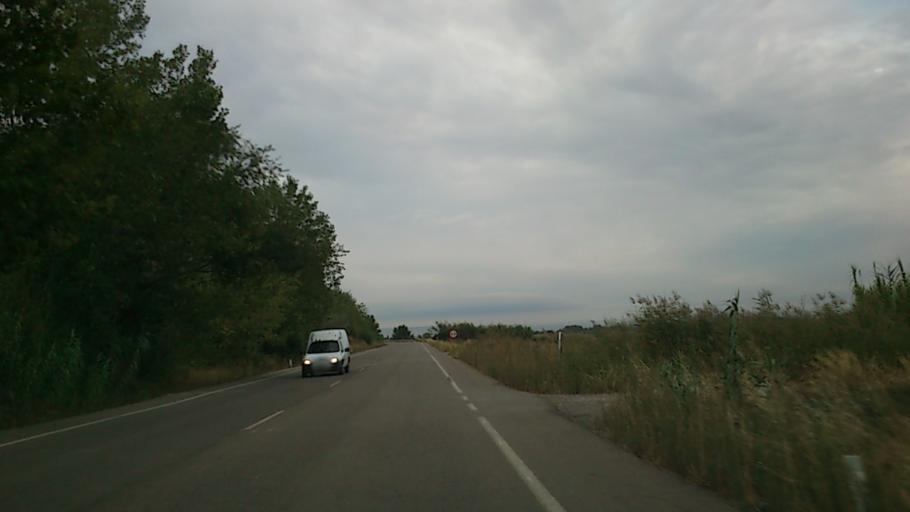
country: ES
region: Aragon
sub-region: Provincia de Zaragoza
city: Villanueva de Gallego
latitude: 41.7871
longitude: -0.7856
